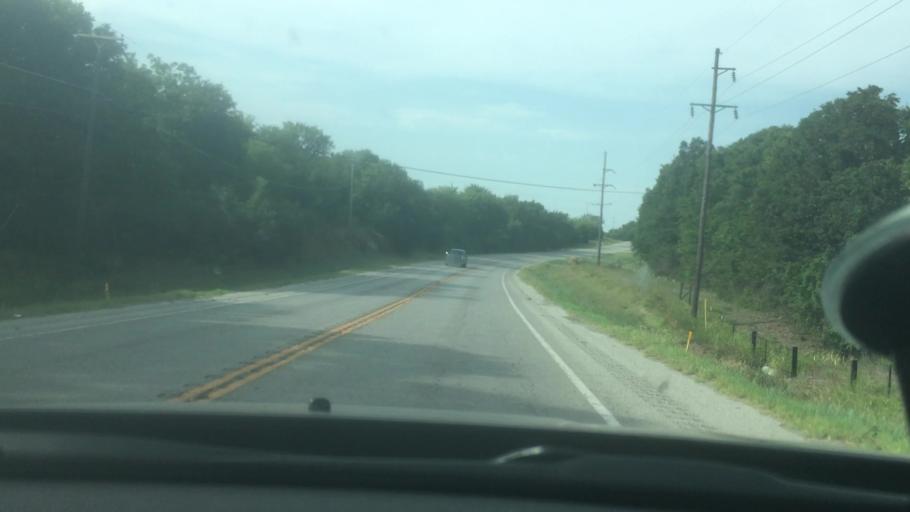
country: US
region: Oklahoma
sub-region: Carter County
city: Ardmore
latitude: 34.1247
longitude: -97.1430
